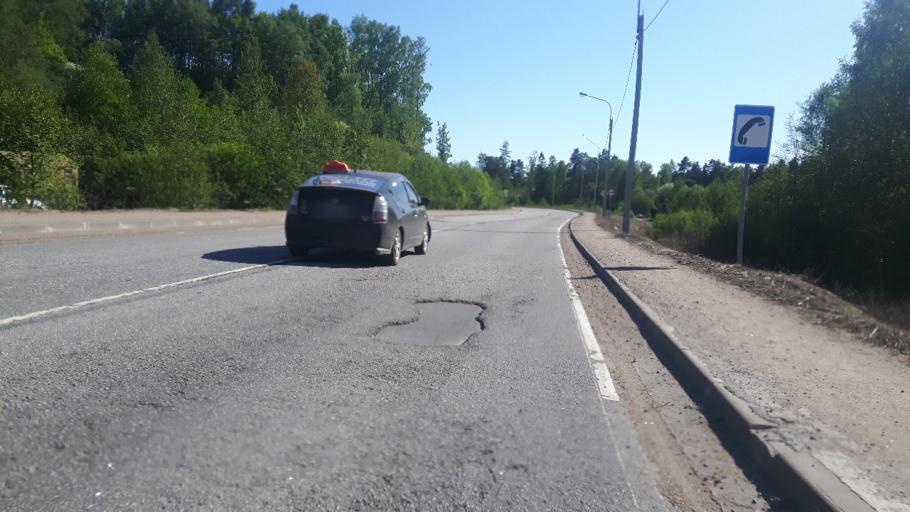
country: RU
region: Leningrad
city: Sosnovyy Bor
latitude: 60.2131
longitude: 29.0073
